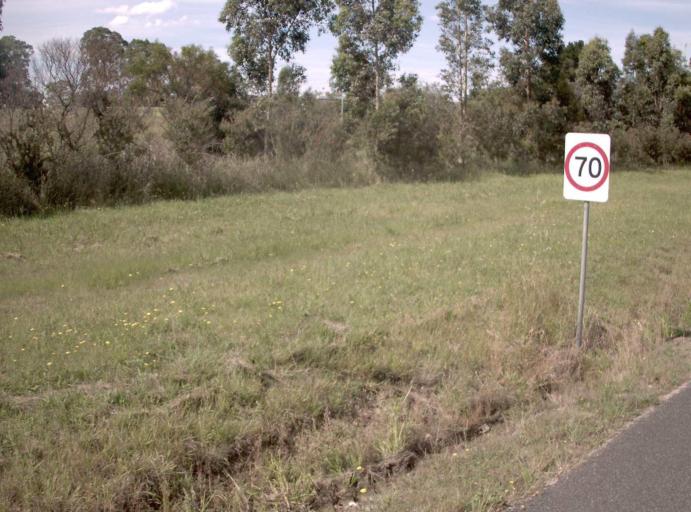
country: AU
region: Victoria
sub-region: East Gippsland
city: Lakes Entrance
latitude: -37.8225
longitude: 147.8542
